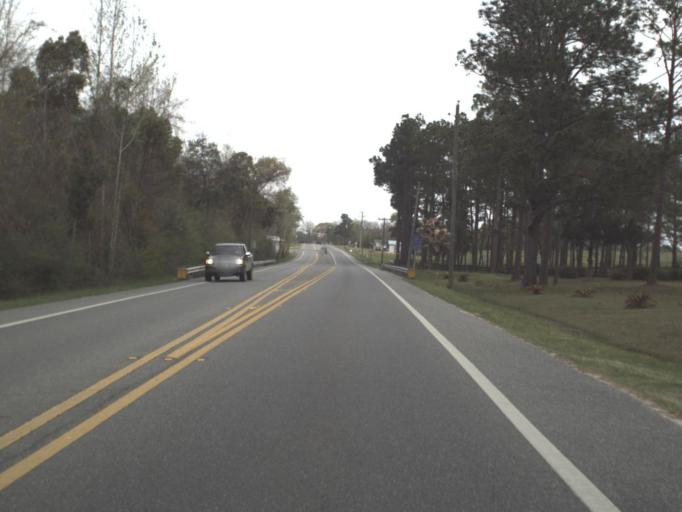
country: US
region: Florida
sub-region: Holmes County
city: Bonifay
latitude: 30.8189
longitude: -85.6706
